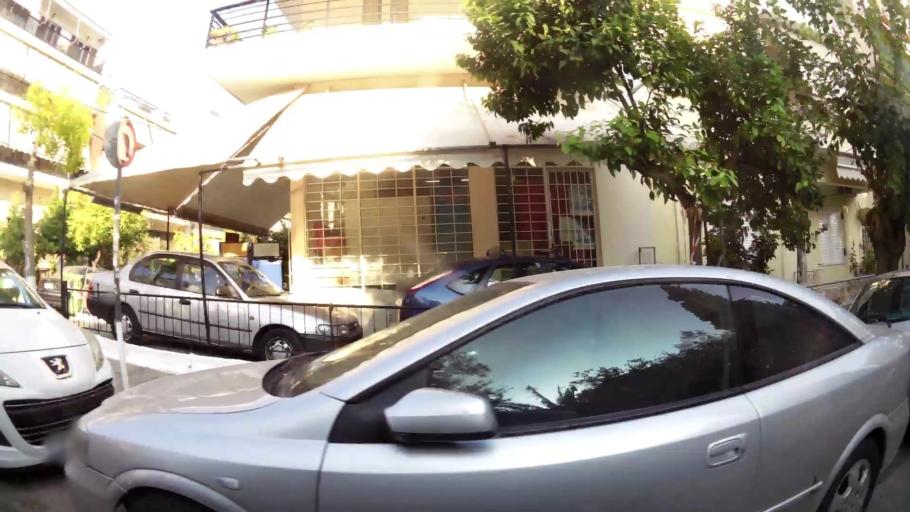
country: GR
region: Attica
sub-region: Nomos Piraios
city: Nikaia
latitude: 37.9679
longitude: 23.6360
